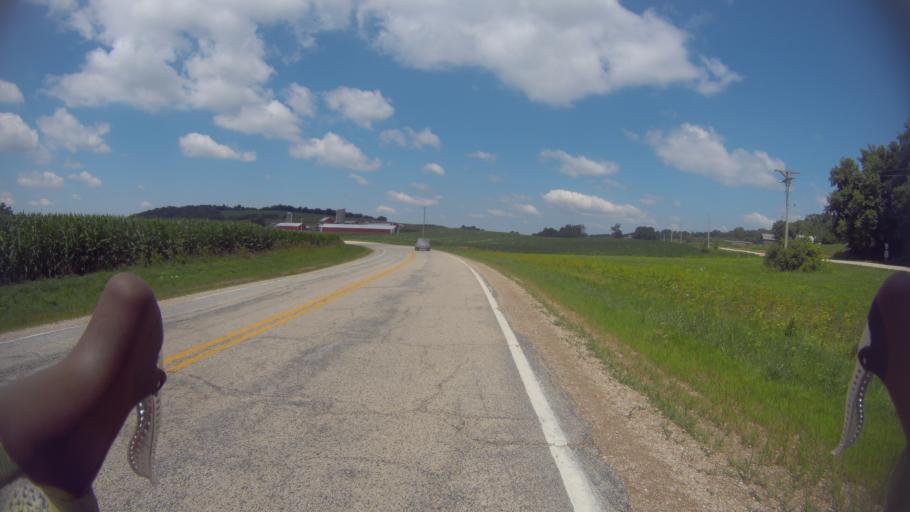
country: US
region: Wisconsin
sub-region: Columbia County
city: Lodi
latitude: 43.2491
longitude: -89.6079
